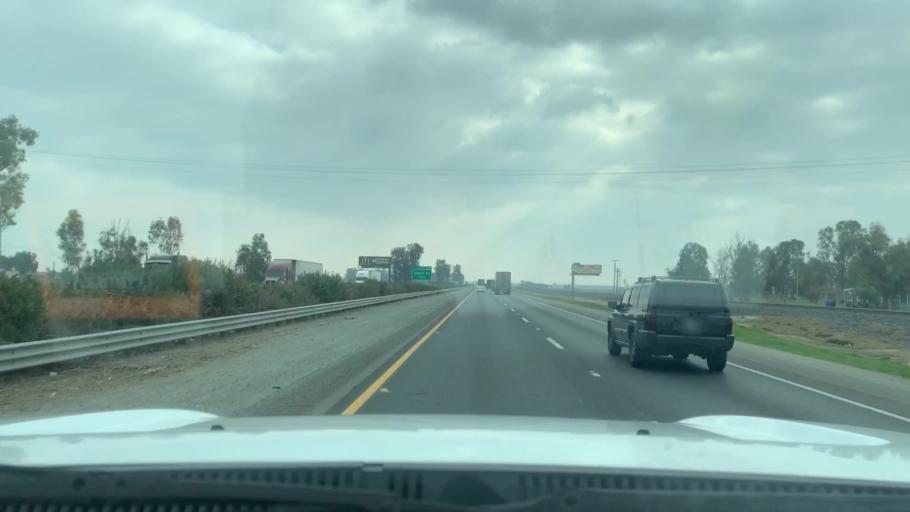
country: US
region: California
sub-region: Tulare County
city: Pixley
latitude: 35.9937
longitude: -119.2995
